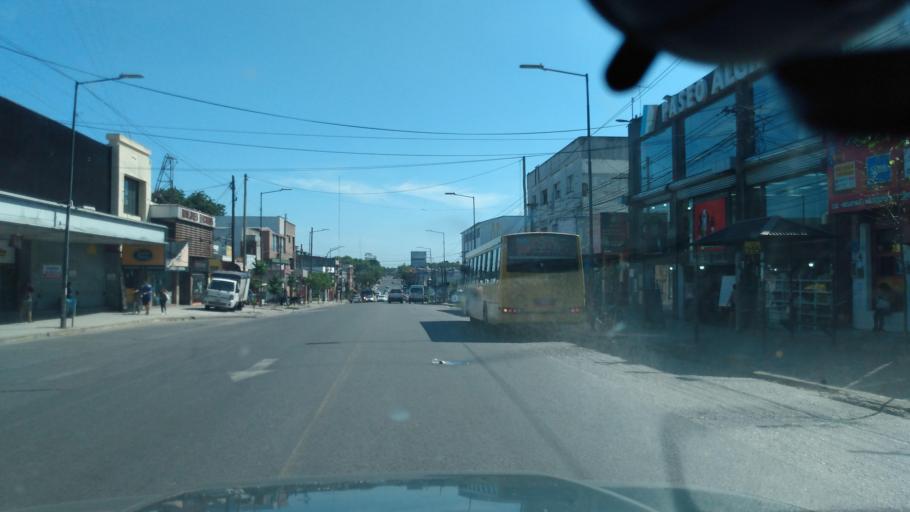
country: AR
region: Buenos Aires
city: Hurlingham
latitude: -34.5445
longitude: -58.7144
